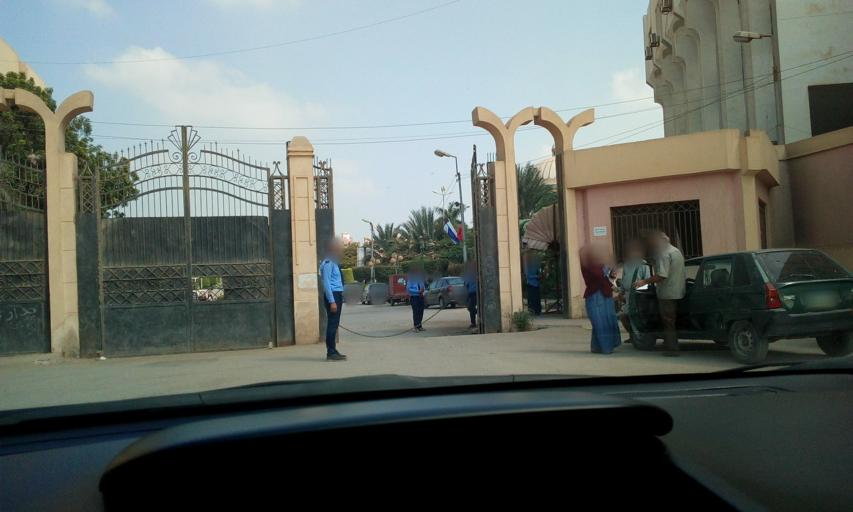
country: EG
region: Muhafazat al Fayyum
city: Al Fayyum
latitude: 29.3190
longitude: 30.8348
